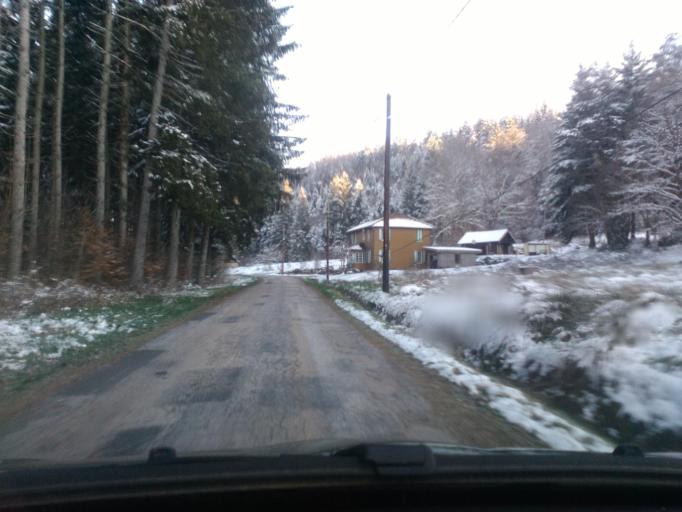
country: FR
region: Lorraine
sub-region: Departement des Vosges
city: Granges-sur-Vologne
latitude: 48.1316
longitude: 6.8279
